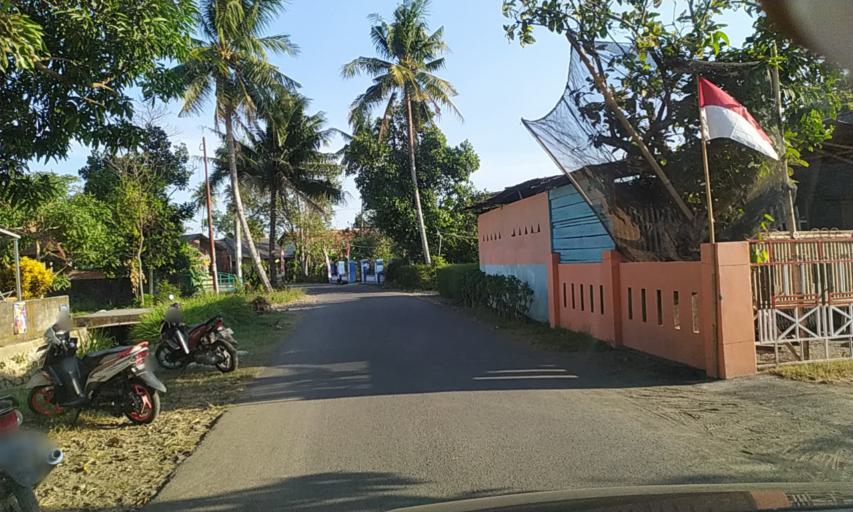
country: ID
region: Central Java
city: Rejanegara
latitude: -7.6778
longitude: 109.0521
